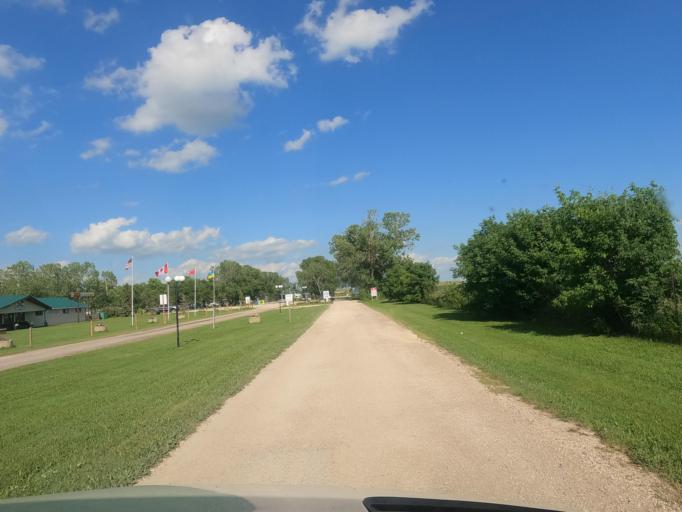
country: CA
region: Manitoba
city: Winnipeg
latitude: 49.8267
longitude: -96.9794
